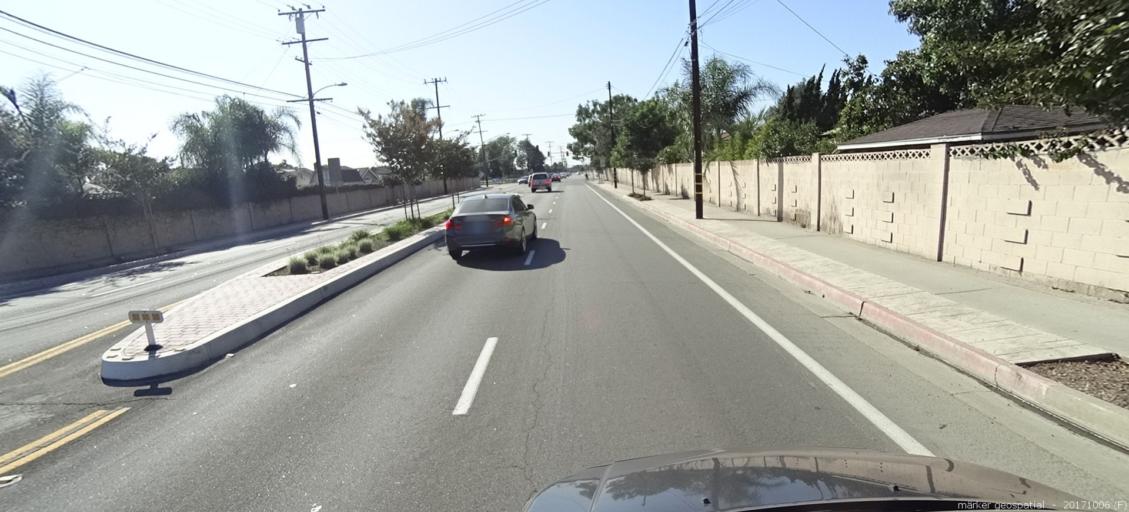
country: US
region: California
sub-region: Orange County
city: Westminster
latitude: 33.7811
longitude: -118.0185
